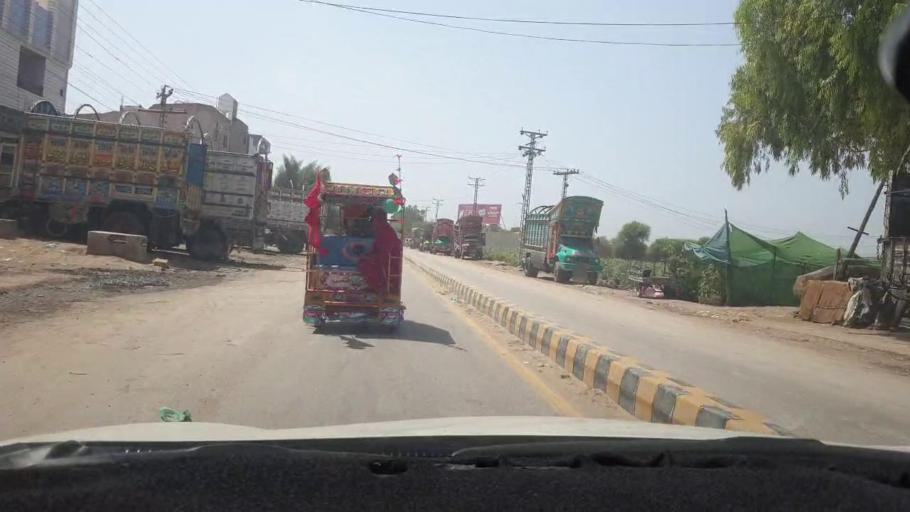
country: PK
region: Sindh
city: Shahdadpur
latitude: 25.9162
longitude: 68.6108
